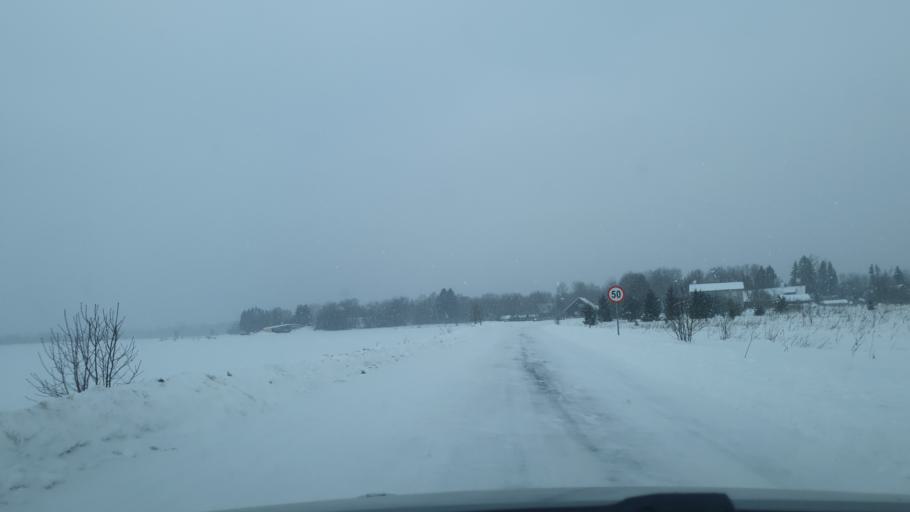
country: EE
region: Harju
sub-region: Maardu linn
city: Maardu
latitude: 59.4568
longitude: 25.0934
